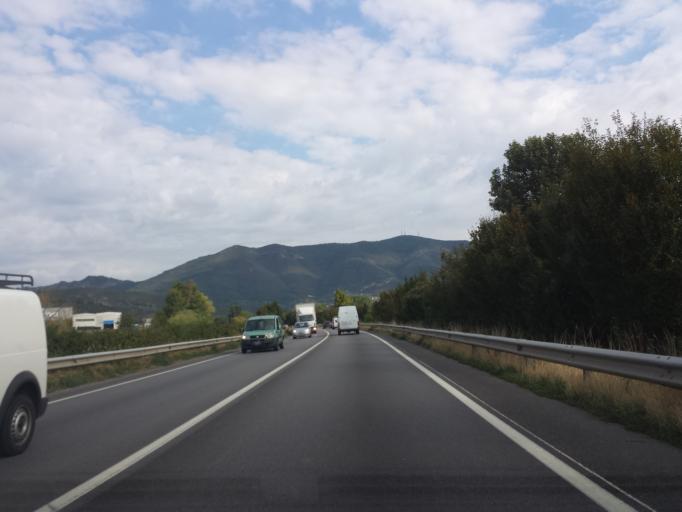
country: IT
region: Lombardy
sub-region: Provincia di Brescia
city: Chiesa
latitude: 45.5675
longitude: 10.4422
